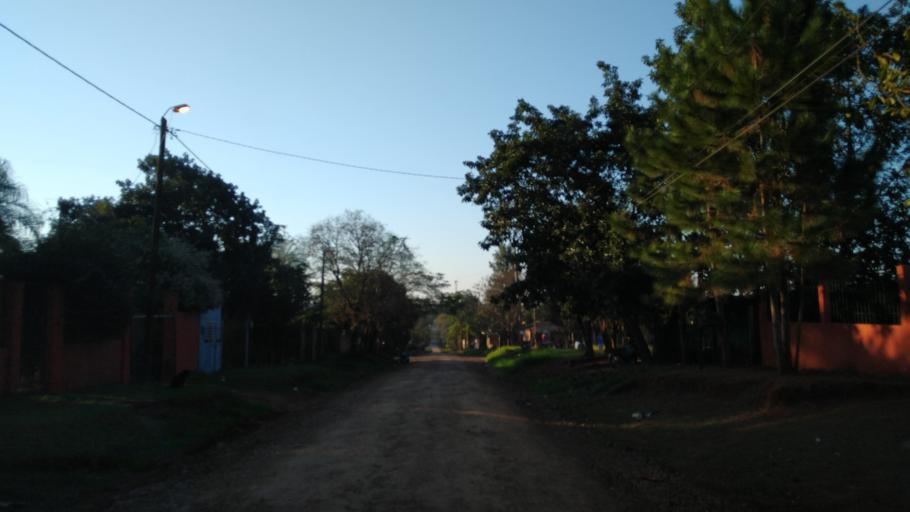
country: AR
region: Misiones
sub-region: Departamento de Capital
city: Posadas
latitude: -27.4240
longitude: -55.9208
